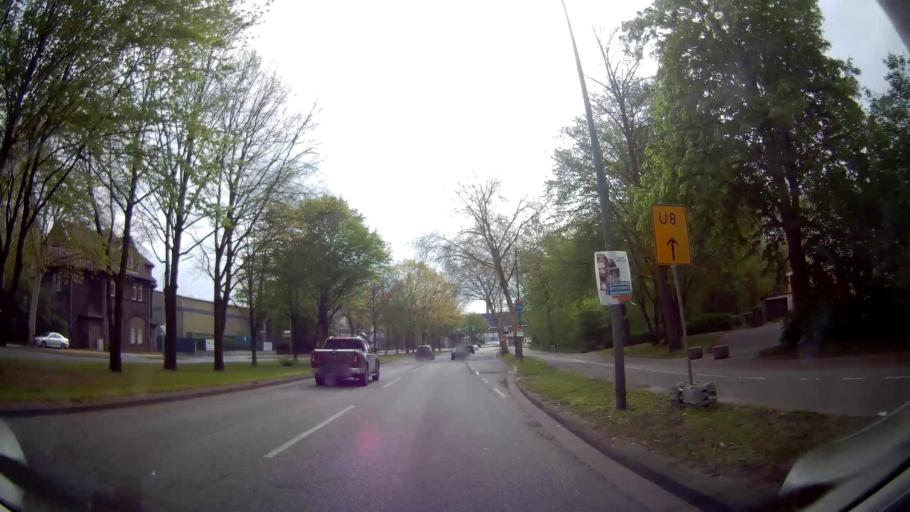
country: DE
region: North Rhine-Westphalia
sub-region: Regierungsbezirk Munster
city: Gelsenkirchen
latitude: 51.5236
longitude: 7.0686
